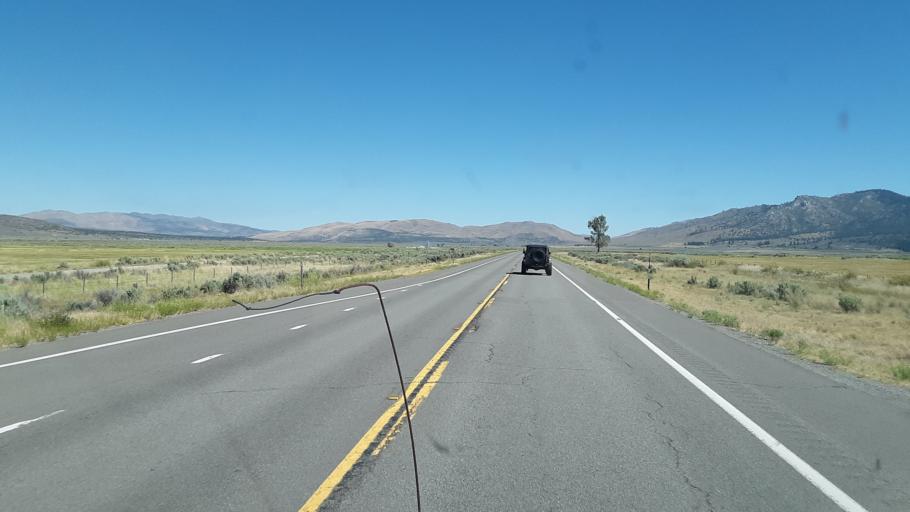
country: US
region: Nevada
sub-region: Washoe County
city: Cold Springs
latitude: 39.9990
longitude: -120.0792
